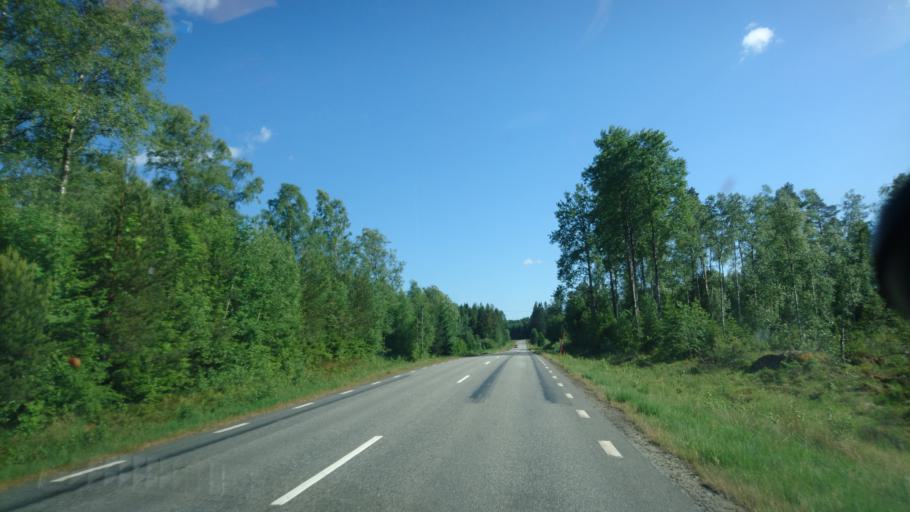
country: SE
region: Skane
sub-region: Osby Kommun
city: Lonsboda
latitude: 56.4509
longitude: 14.2354
